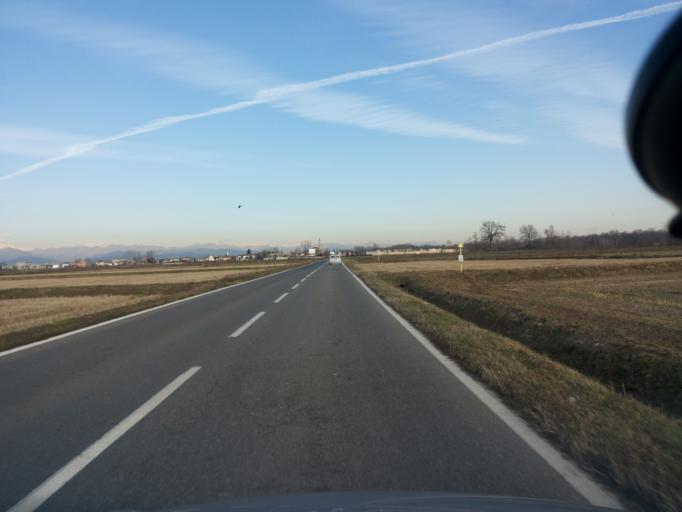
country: IT
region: Piedmont
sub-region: Provincia di Vercelli
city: Arborio
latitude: 45.4838
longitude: 8.3884
